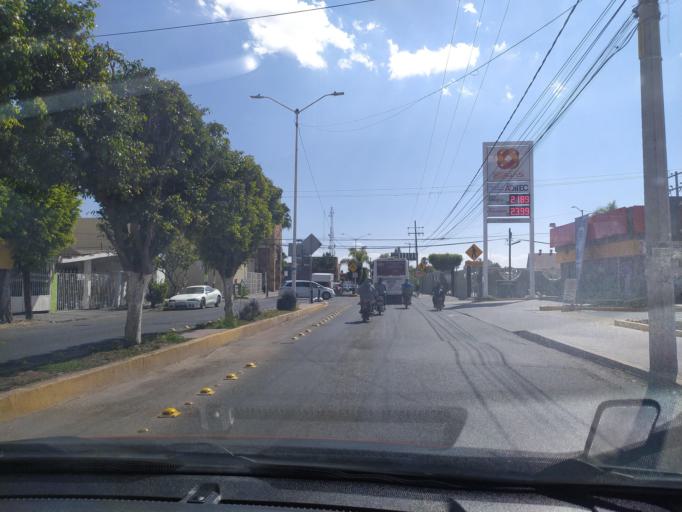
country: LA
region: Oudomxai
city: Muang La
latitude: 21.0234
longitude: 101.8517
